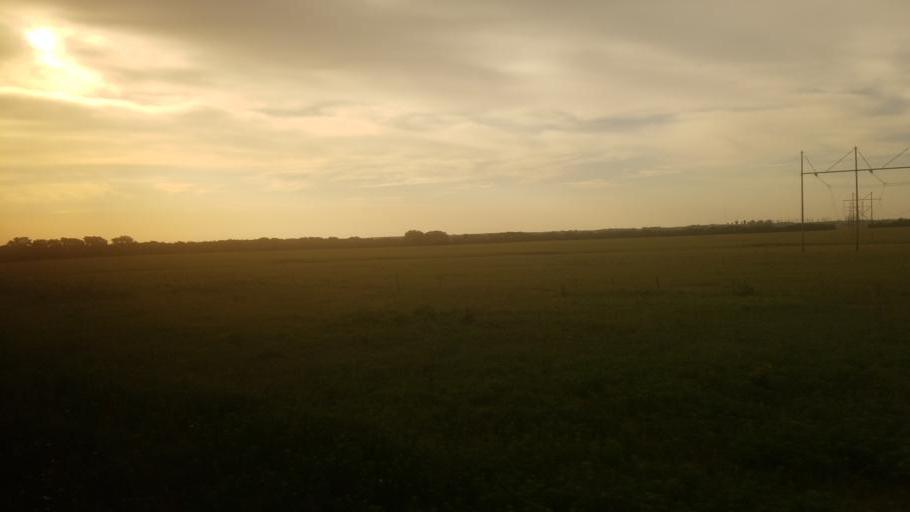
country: US
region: Kansas
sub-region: Lyon County
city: Emporia
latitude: 38.4572
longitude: -96.0871
